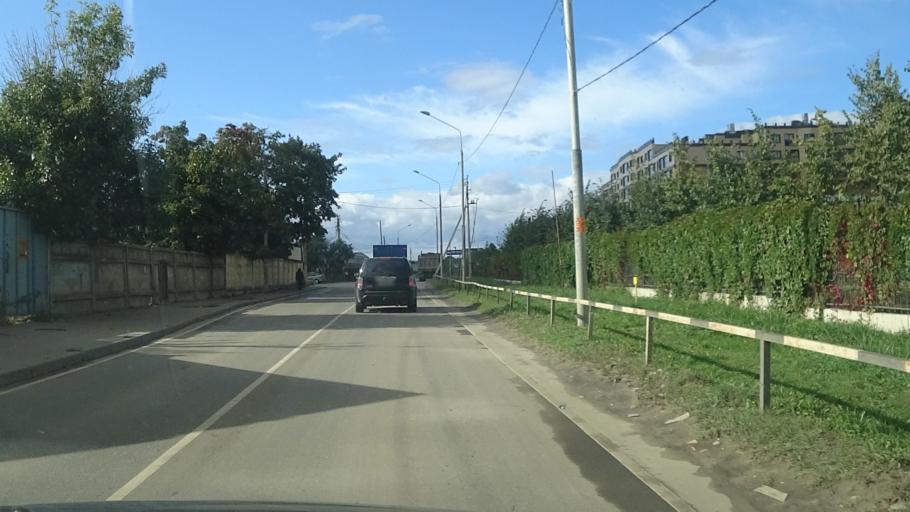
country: RU
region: Moskovskaya
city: Kommunarka
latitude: 55.5669
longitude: 37.4426
